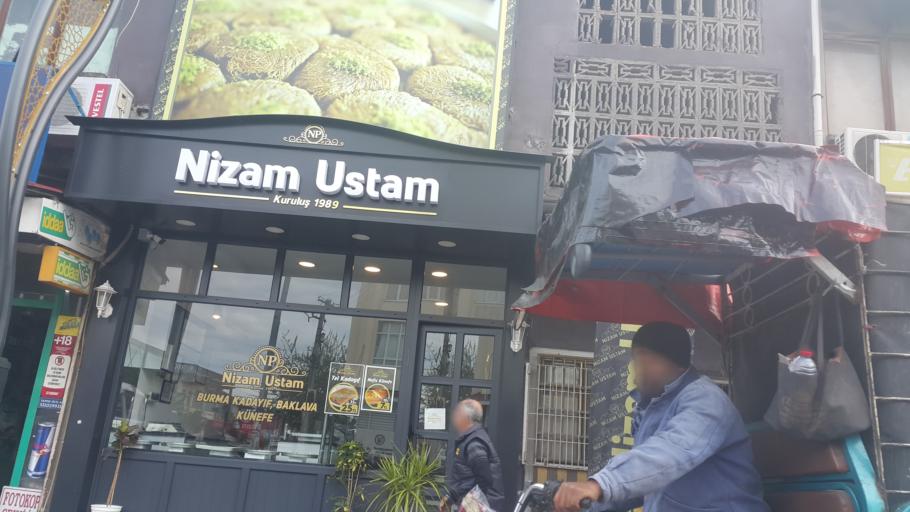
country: TR
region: Mersin
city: Tarsus
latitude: 36.9193
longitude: 34.9007
